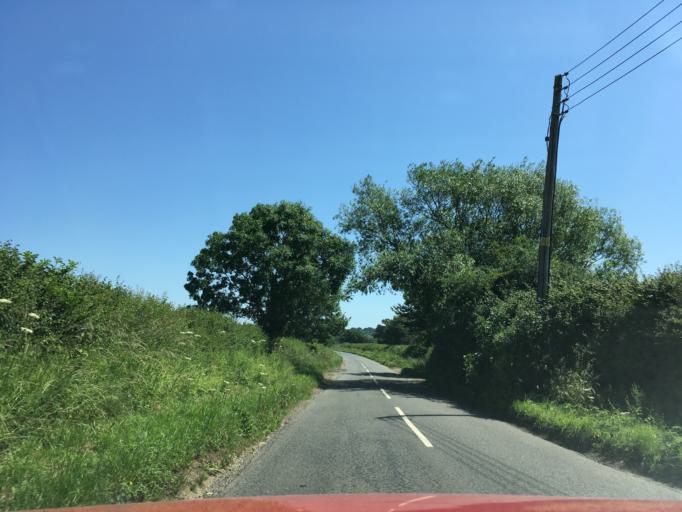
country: GB
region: England
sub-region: Milton Keynes
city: Calverton
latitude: 52.0035
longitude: -0.8581
